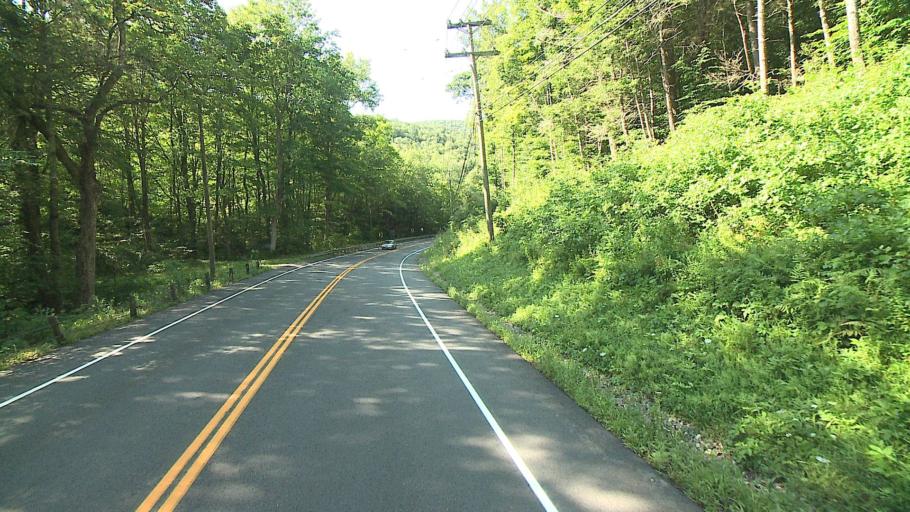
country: US
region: Connecticut
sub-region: Litchfield County
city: New Preston
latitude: 41.8329
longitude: -73.3477
